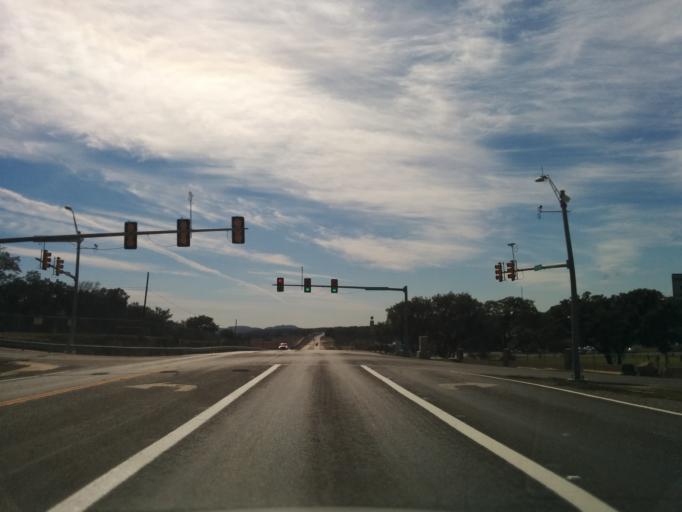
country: US
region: Texas
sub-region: Bexar County
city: Fair Oaks Ranch
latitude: 29.7314
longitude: -98.6235
